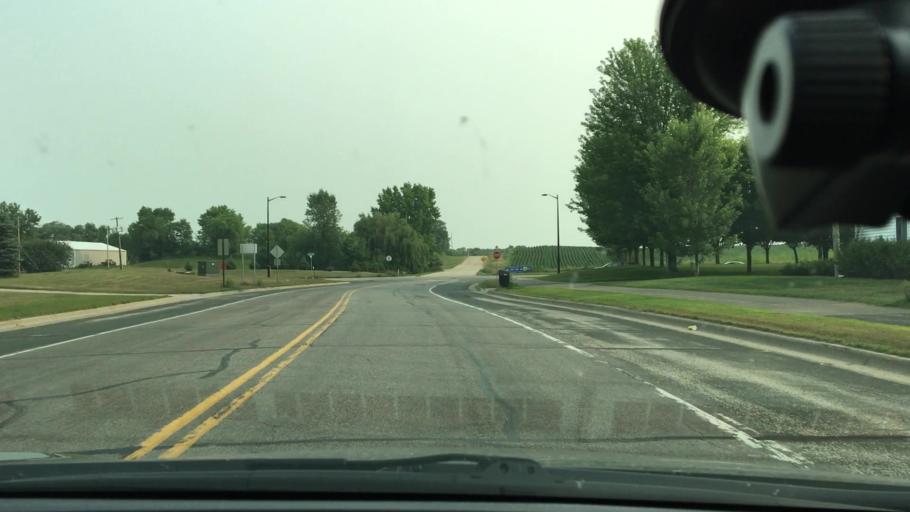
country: US
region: Minnesota
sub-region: Wright County
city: Otsego
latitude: 45.2534
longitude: -93.5914
